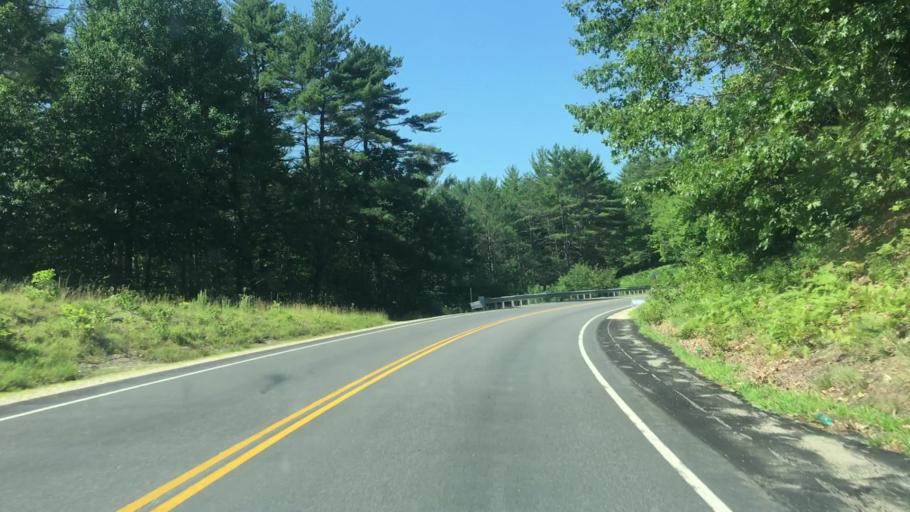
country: US
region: New Hampshire
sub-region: Merrimack County
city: Contoocook
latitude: 43.1863
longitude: -71.7495
